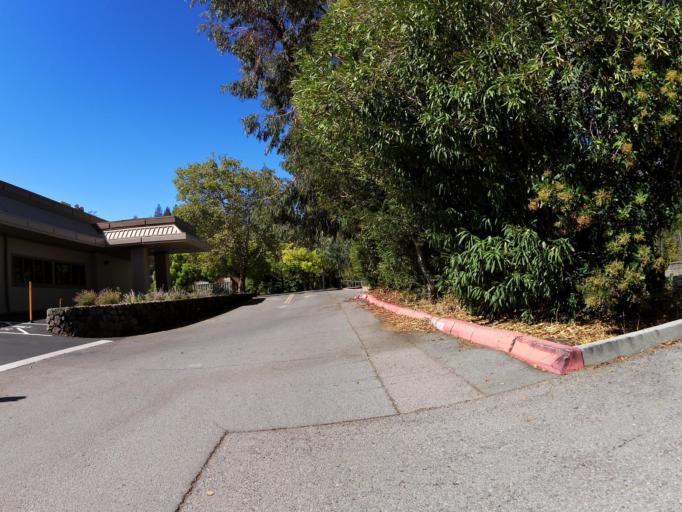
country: US
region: California
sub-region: Marin County
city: Kentfield
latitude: 37.9539
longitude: -122.5481
